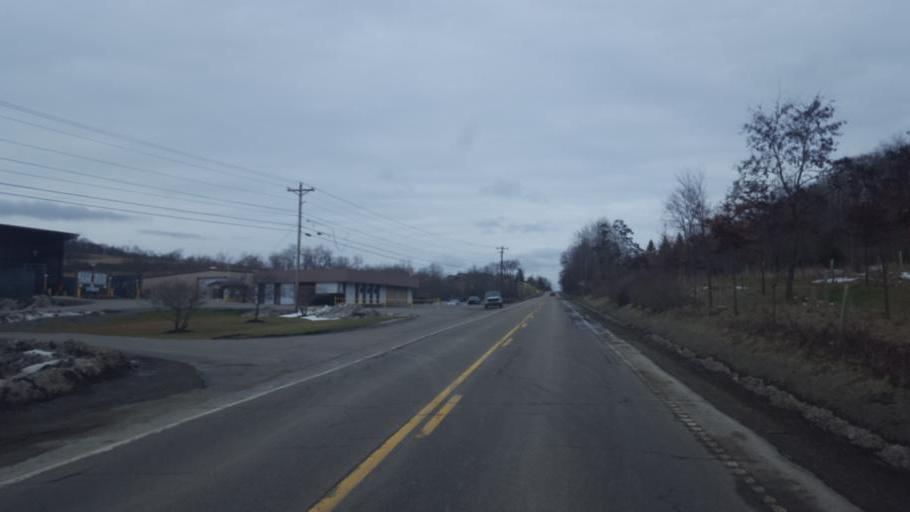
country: US
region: Pennsylvania
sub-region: Potter County
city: Coudersport
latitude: 41.8753
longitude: -77.8335
